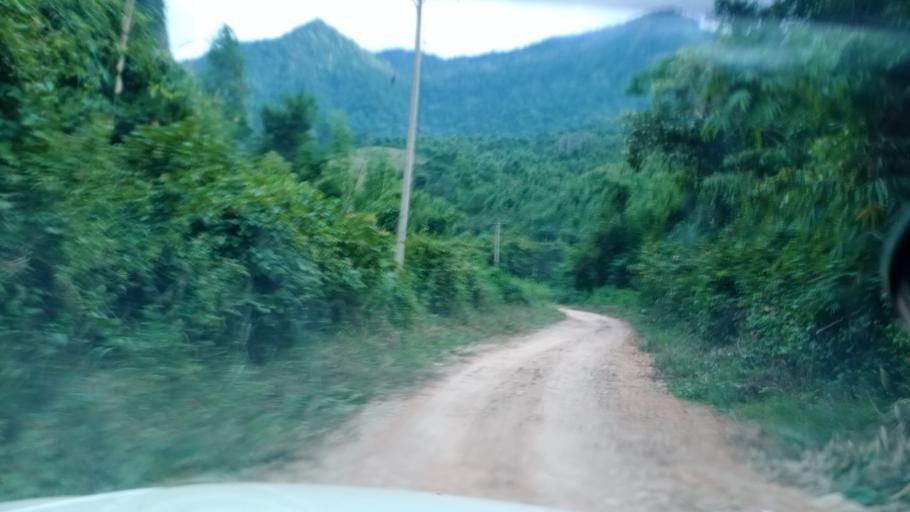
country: TH
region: Changwat Bueng Kan
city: Pak Khat
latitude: 18.7255
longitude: 103.2568
